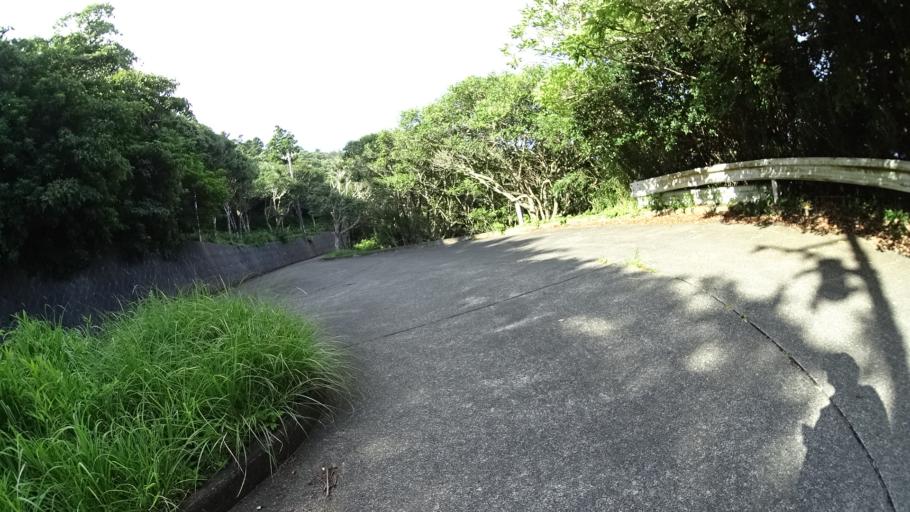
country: JP
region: Shizuoka
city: Shimoda
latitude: 34.5246
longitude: 139.2760
